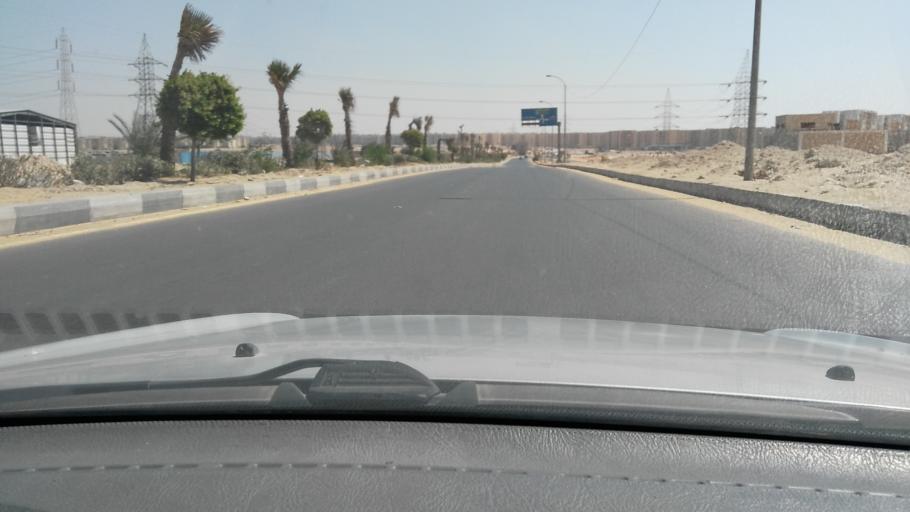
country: EG
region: Al Jizah
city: Madinat Sittah Uktubar
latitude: 29.9089
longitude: 30.9262
